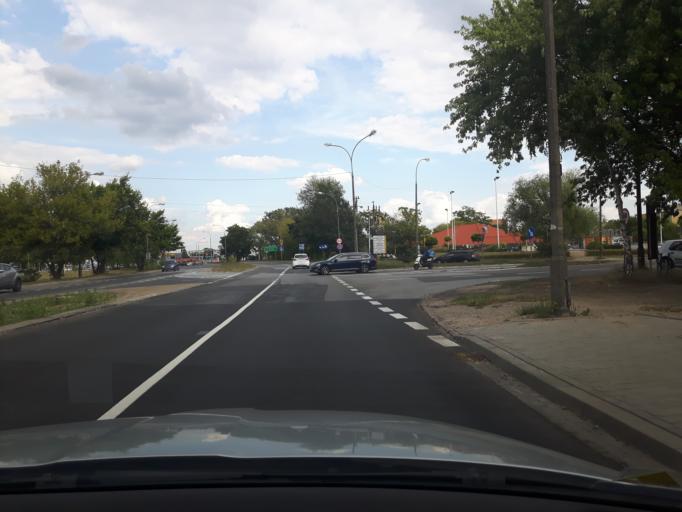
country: PL
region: Masovian Voivodeship
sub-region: Powiat piaseczynski
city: Piaseczno
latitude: 52.0810
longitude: 21.0208
